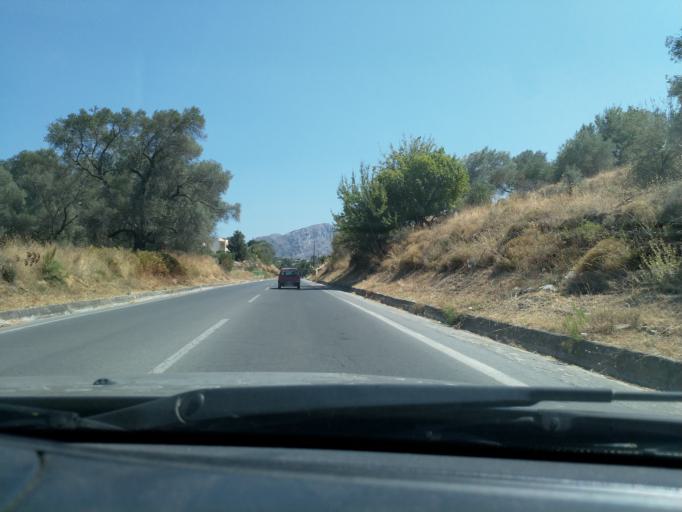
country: GR
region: Crete
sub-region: Nomos Rethymnis
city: Atsipopoulon
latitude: 35.2218
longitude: 24.4942
